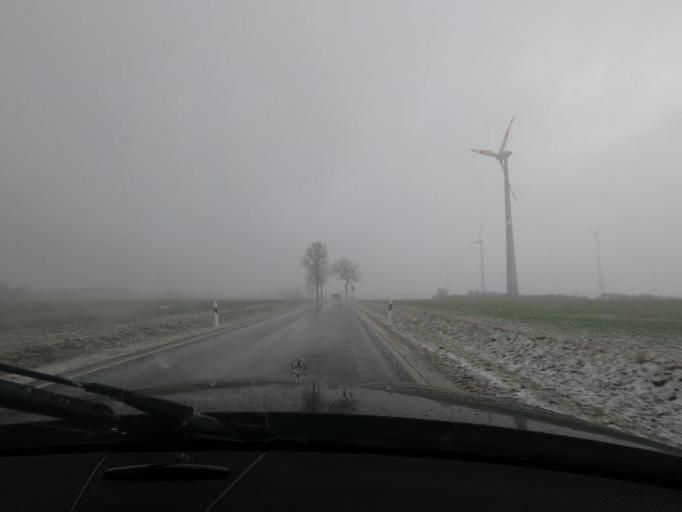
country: DE
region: Thuringia
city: Buttstedt
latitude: 51.2454
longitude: 10.2810
